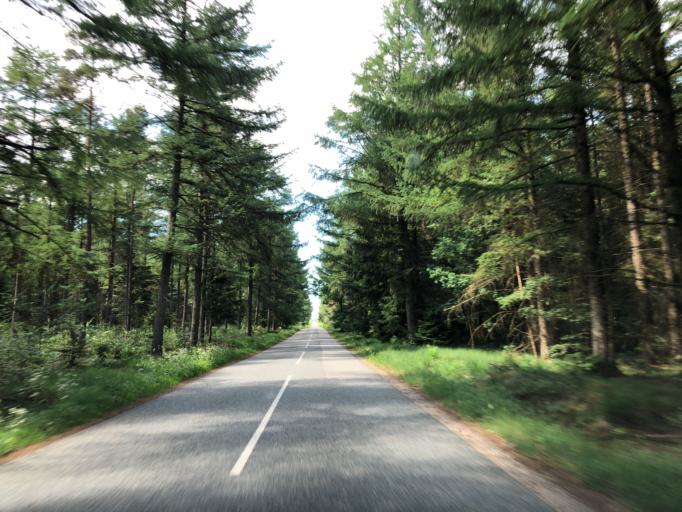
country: DK
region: Central Jutland
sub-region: Herning Kommune
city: Lind
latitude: 56.0425
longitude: 8.9342
